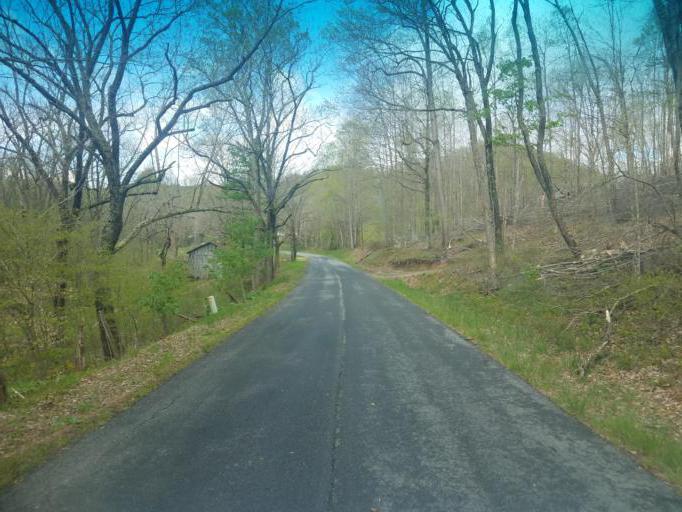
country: US
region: Virginia
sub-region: Smyth County
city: Atkins
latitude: 36.9745
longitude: -81.3940
